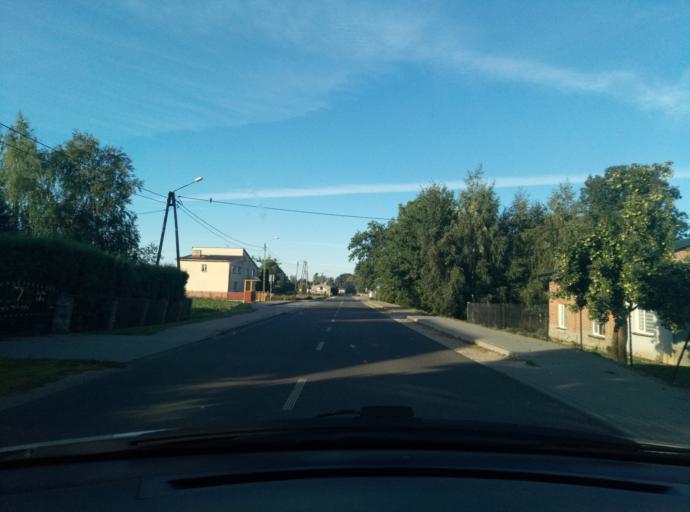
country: PL
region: Kujawsko-Pomorskie
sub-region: Powiat golubsko-dobrzynski
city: Kowalewo Pomorskie
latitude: 53.2019
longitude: 18.9168
